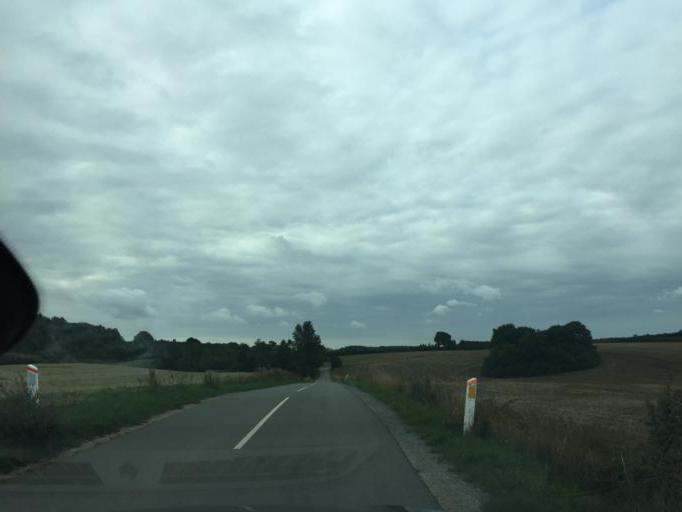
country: DK
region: South Denmark
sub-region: Assens Kommune
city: Tommerup Stationsby
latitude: 55.3717
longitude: 10.1693
